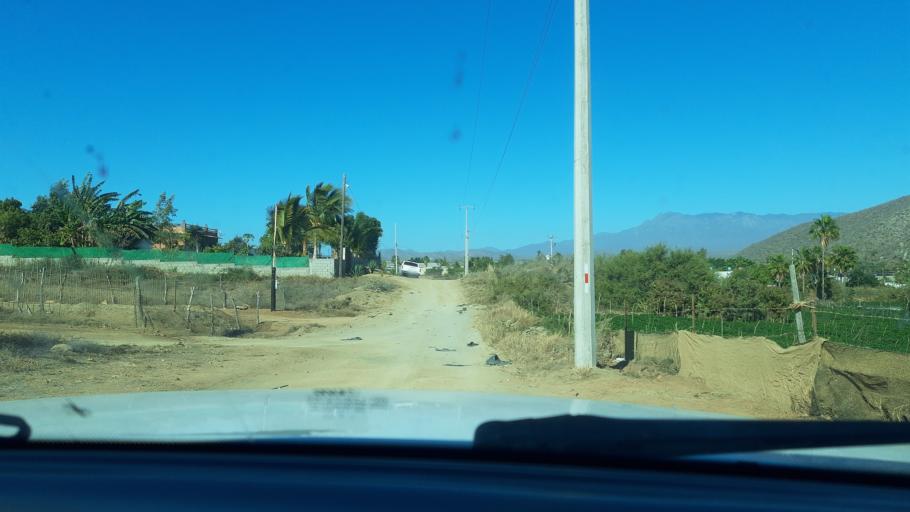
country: MX
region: Baja California Sur
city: Todos Santos
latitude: 23.4733
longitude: -110.2177
